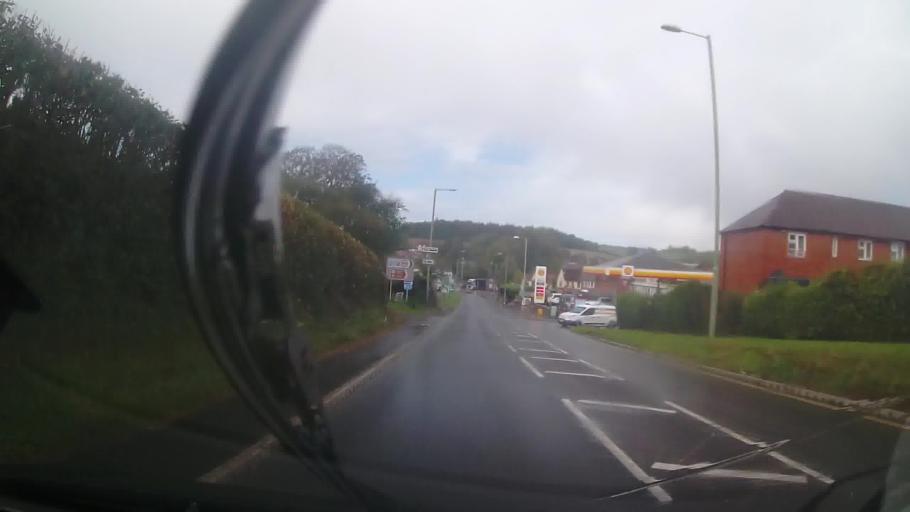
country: GB
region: England
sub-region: Shropshire
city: Much Wenlock
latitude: 52.5933
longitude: -2.5589
